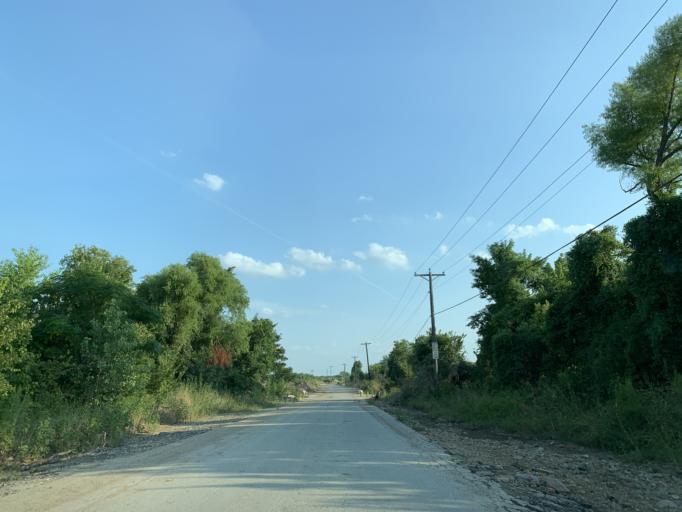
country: US
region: Texas
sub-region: Tarrant County
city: Hurst
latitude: 32.7978
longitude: -97.1693
